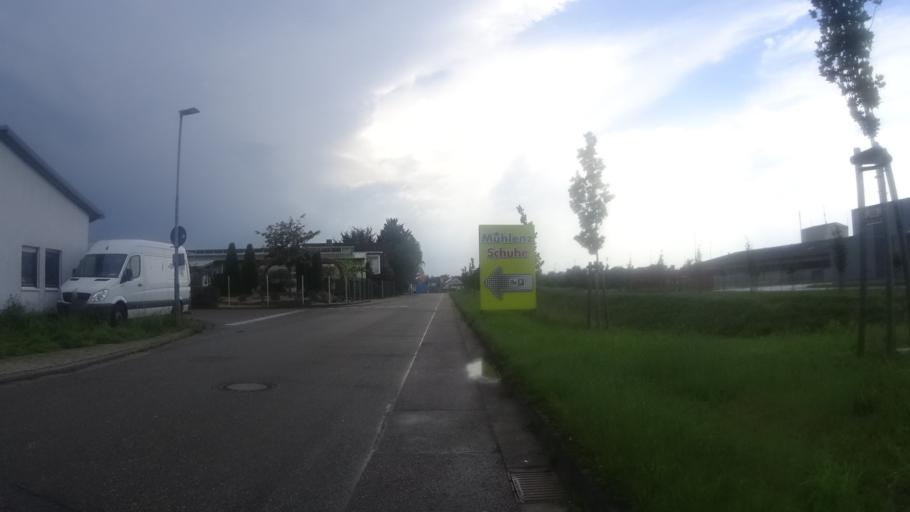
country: DE
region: Baden-Wuerttemberg
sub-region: Karlsruhe Region
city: Otigheim
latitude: 48.8847
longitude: 8.2420
